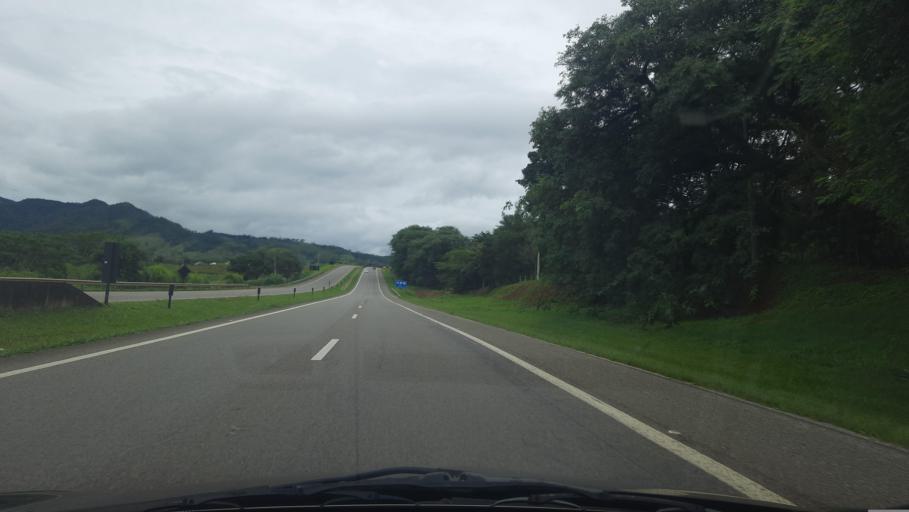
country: BR
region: Sao Paulo
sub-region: Sao Joao Da Boa Vista
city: Sao Joao da Boa Vista
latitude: -21.9583
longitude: -46.7323
